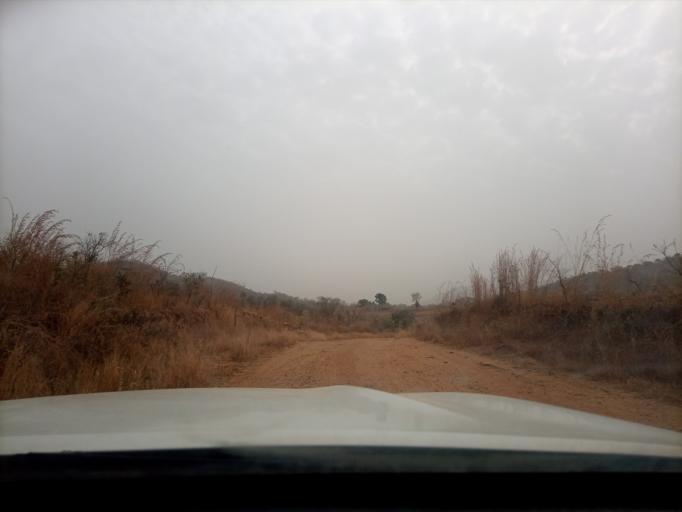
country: ET
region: Oromiya
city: Mendi
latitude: 10.1934
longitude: 35.0599
